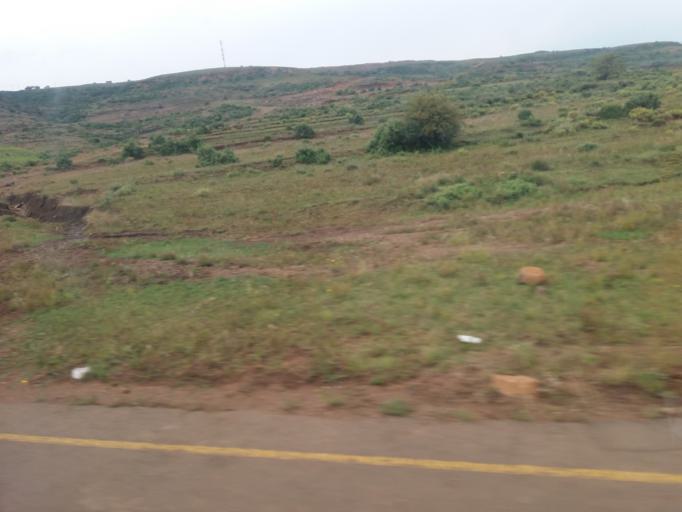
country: LS
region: Berea
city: Teyateyaneng
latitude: -29.3240
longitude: 27.7624
